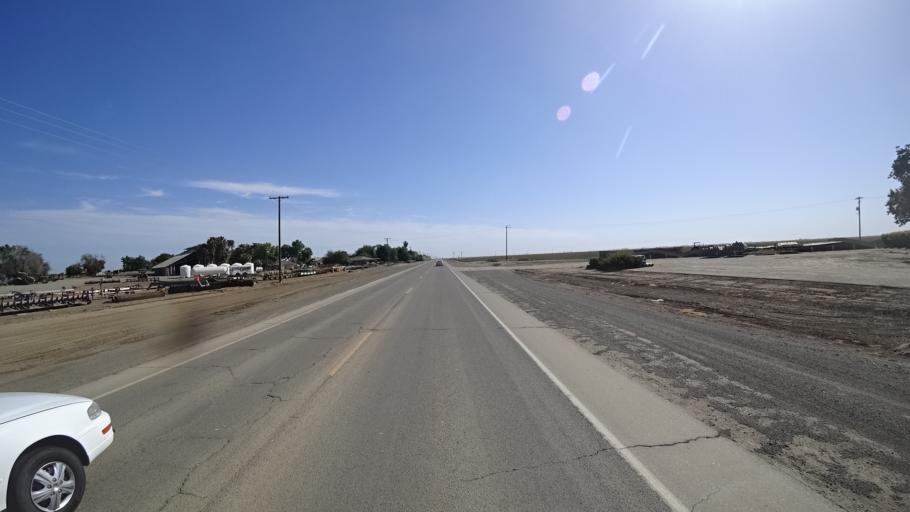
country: US
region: California
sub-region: Kings County
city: Lemoore Station
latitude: 36.1778
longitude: -119.9602
